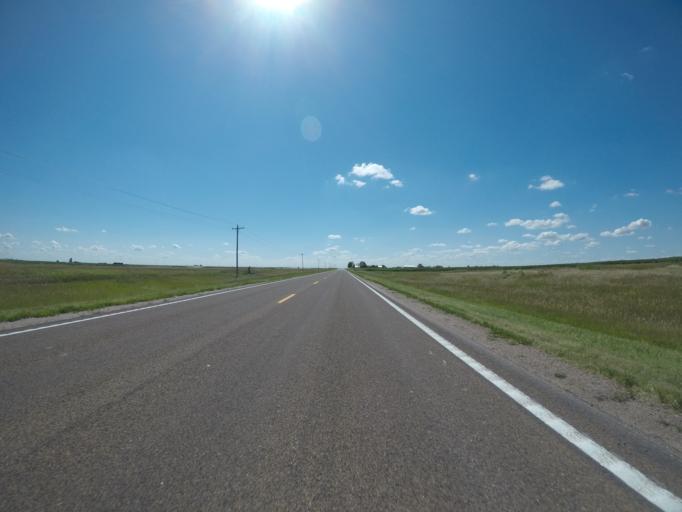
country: US
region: Nebraska
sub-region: Chase County
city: Imperial
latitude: 40.5376
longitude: -101.8472
